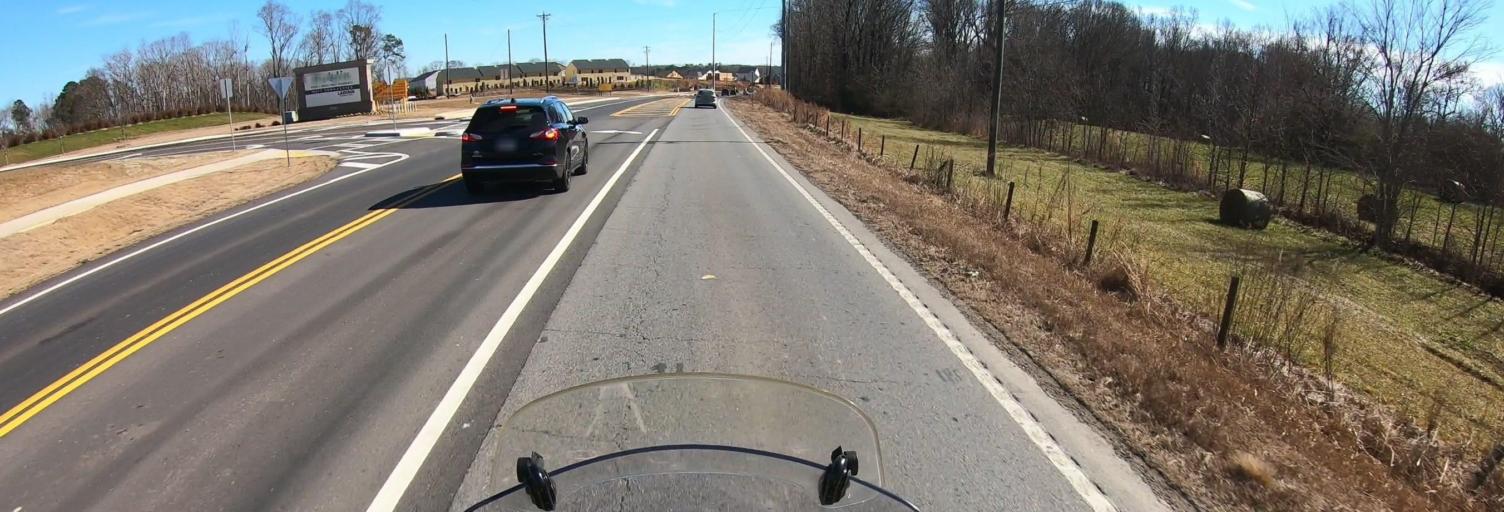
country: US
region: Georgia
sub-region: Forsyth County
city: Cumming
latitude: 34.2935
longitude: -84.1534
